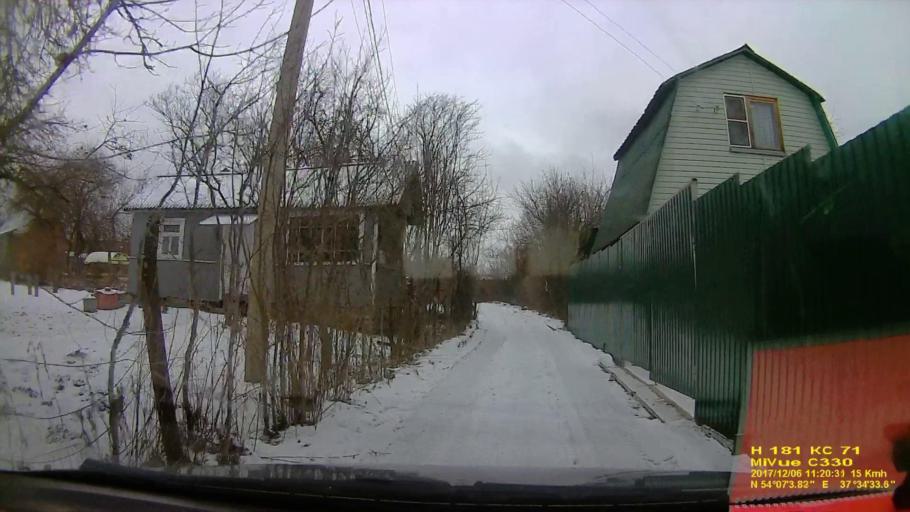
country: RU
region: Tula
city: Mendeleyevskiy
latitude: 54.1178
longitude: 37.5759
